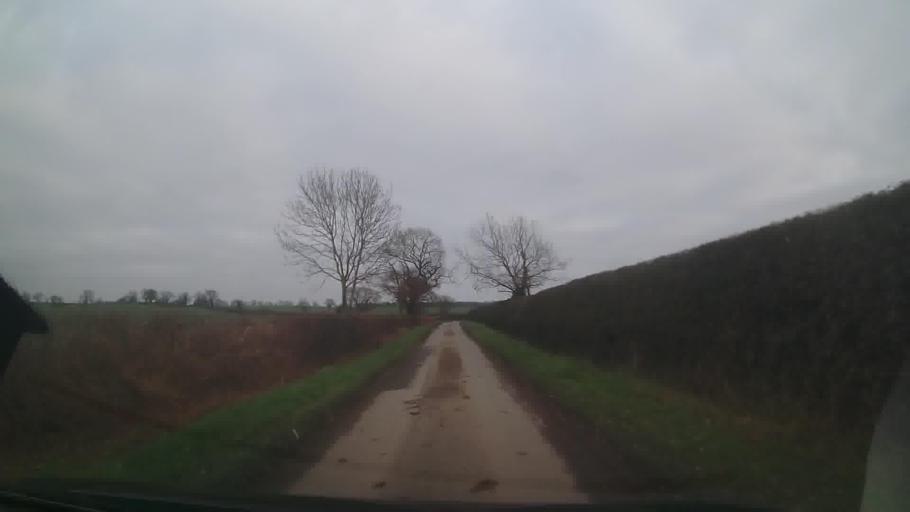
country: GB
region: England
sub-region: Shropshire
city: Petton
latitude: 52.8016
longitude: -2.8122
